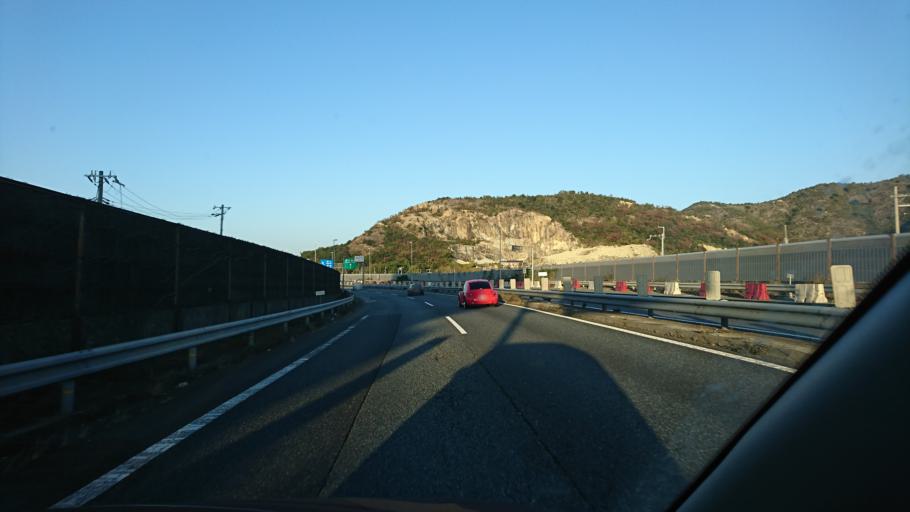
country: JP
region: Hyogo
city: Kakogawacho-honmachi
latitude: 34.7916
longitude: 134.8047
